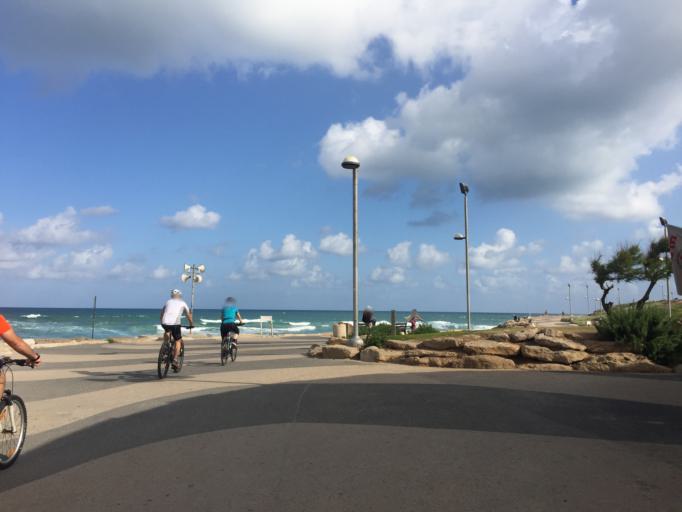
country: IL
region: Tel Aviv
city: Yafo
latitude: 32.0615
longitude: 34.7600
